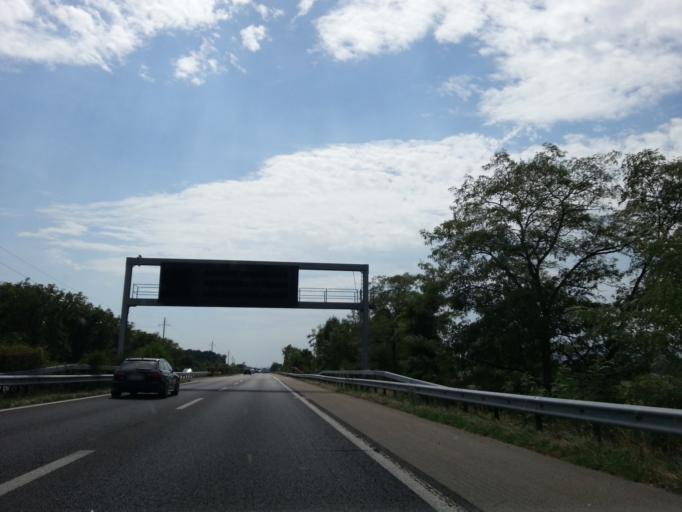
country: CH
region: Geneva
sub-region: Geneva
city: Bellevue
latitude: 46.2712
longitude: 6.1379
